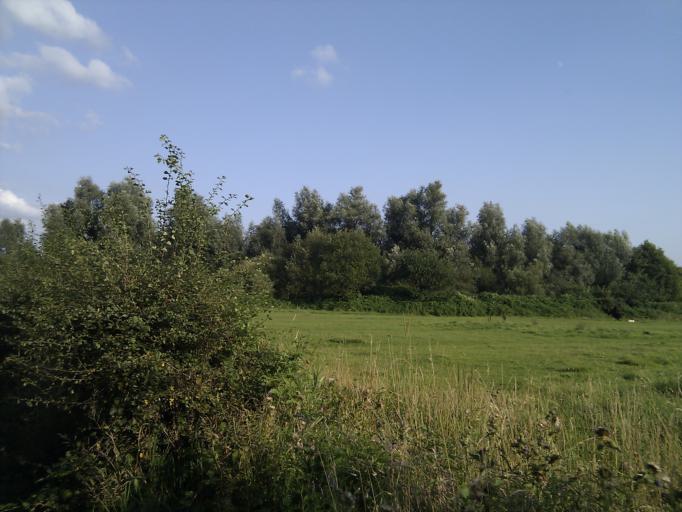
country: NL
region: Utrecht
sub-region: Gemeente De Bilt
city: De Bilt
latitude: 52.0968
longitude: 5.1796
